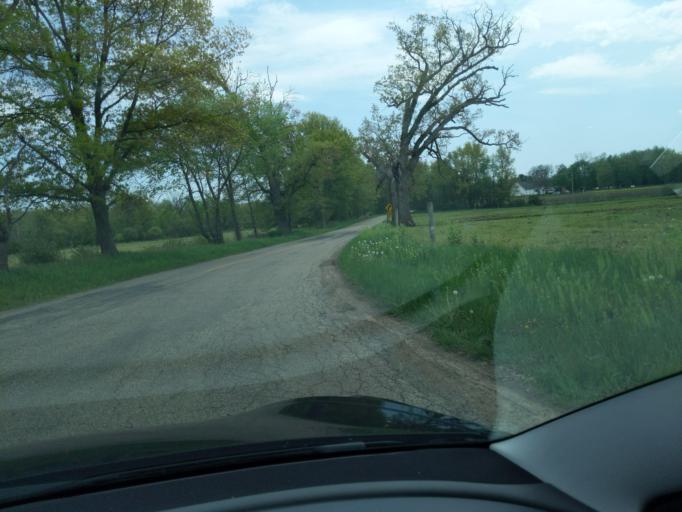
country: US
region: Michigan
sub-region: Ingham County
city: Leslie
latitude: 42.5040
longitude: -84.3422
